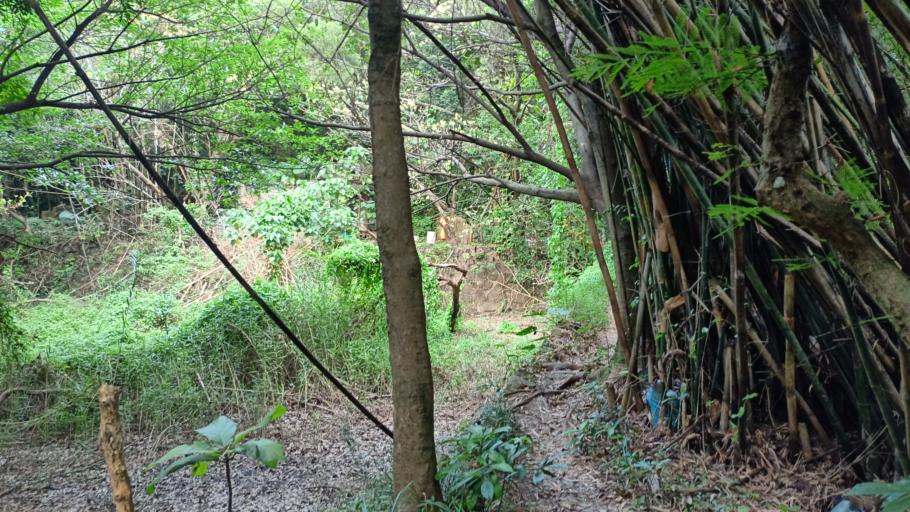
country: HK
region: Tsuen Wan
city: Tsuen Wan
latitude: 22.3352
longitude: 114.0564
